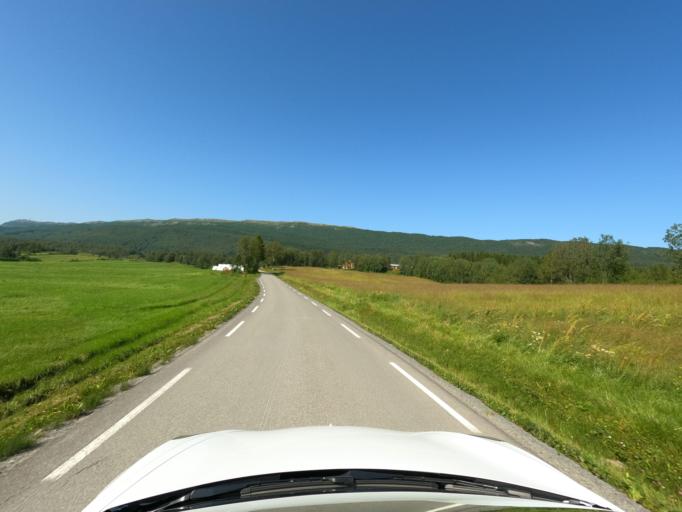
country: NO
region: Nordland
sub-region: Ballangen
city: Ballangen
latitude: 68.3448
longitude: 16.8124
